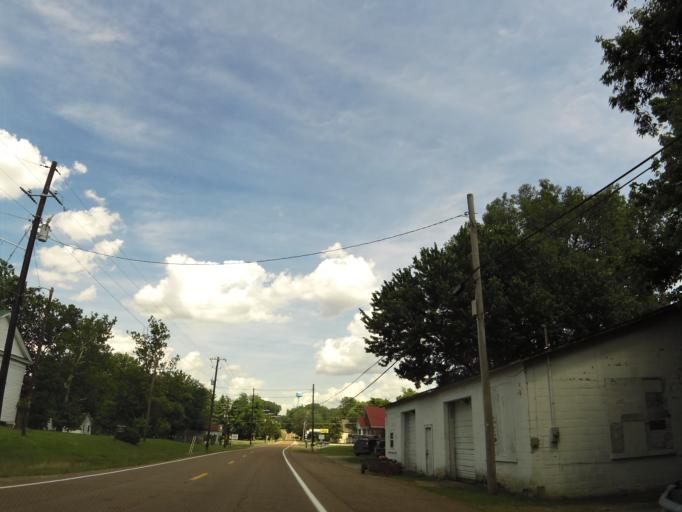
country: US
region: Tennessee
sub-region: Dyer County
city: Newbern
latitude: 36.0238
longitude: -89.2842
